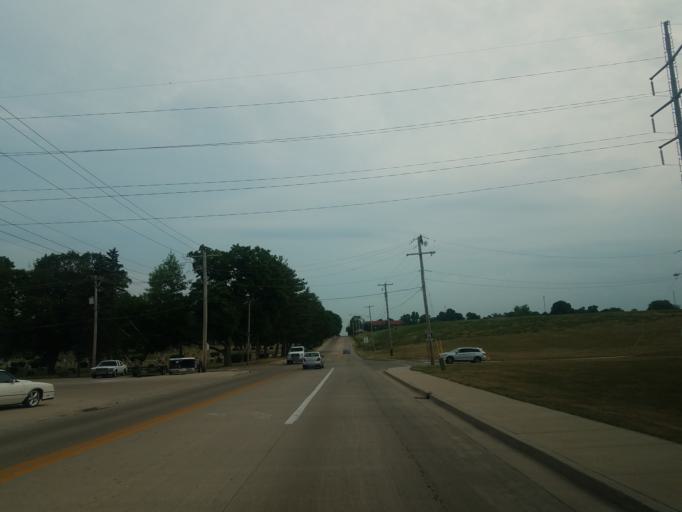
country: US
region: Illinois
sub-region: McLean County
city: Bloomington
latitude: 40.4638
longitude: -89.0061
